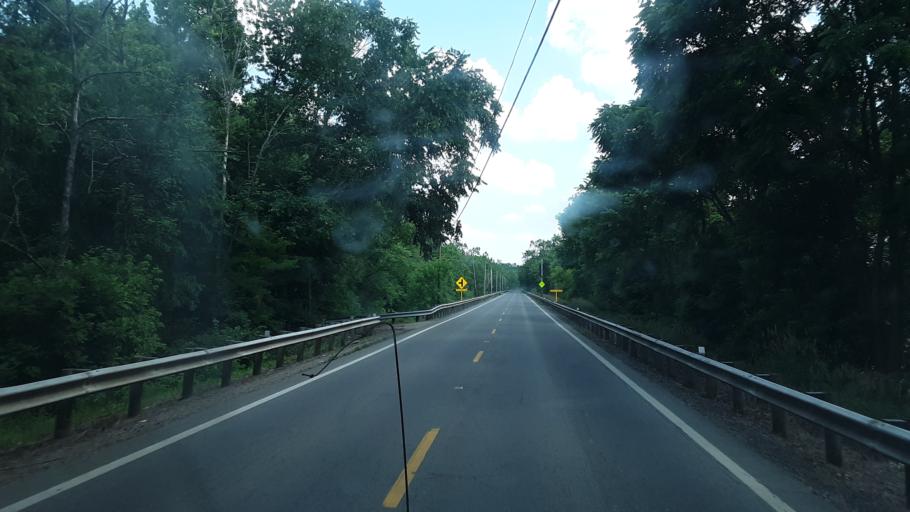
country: US
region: Ohio
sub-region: Tuscarawas County
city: Dover
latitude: 40.5999
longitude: -81.4136
